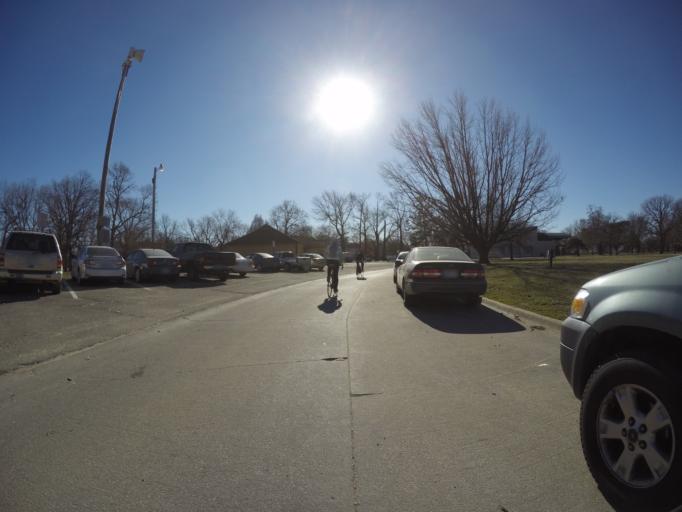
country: US
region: Kansas
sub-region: Riley County
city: Manhattan
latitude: 39.1832
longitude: -96.5745
